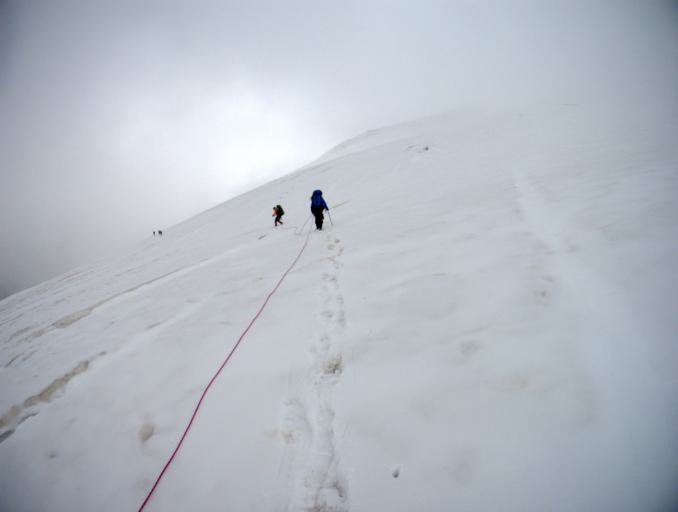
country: RU
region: Kabardino-Balkariya
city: Terskol
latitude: 43.3804
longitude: 42.4608
